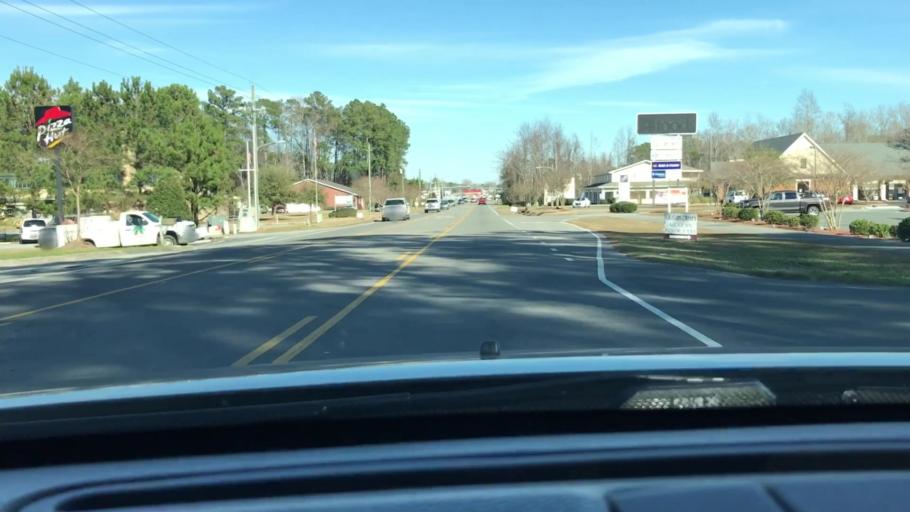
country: US
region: North Carolina
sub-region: Brunswick County
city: Shallotte
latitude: 33.9665
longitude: -78.3939
